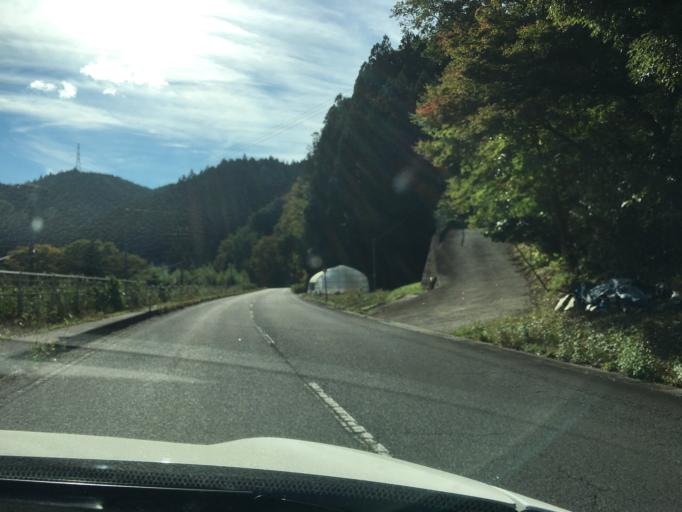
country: JP
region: Fukushima
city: Ishikawa
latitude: 37.1210
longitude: 140.5698
